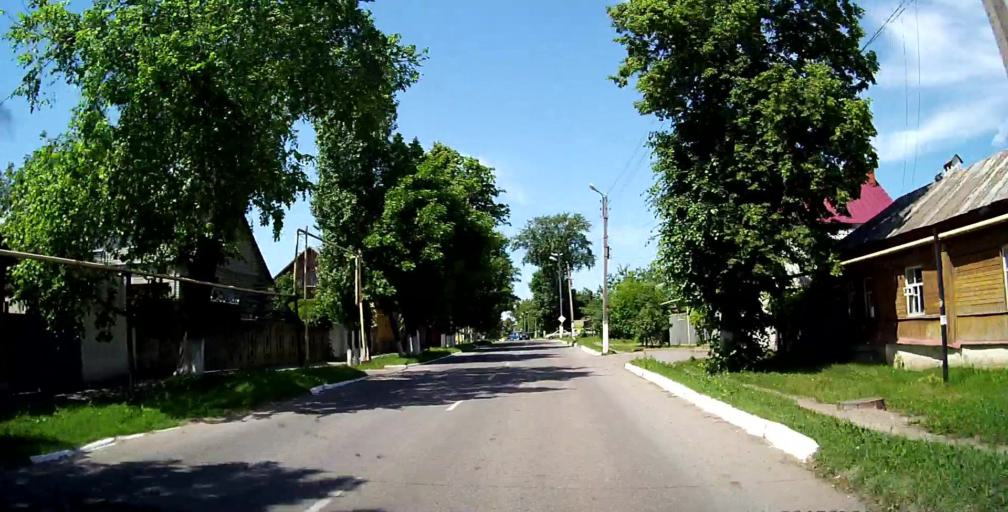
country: RU
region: Lipetsk
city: Chaplygin
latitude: 53.2433
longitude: 39.9713
